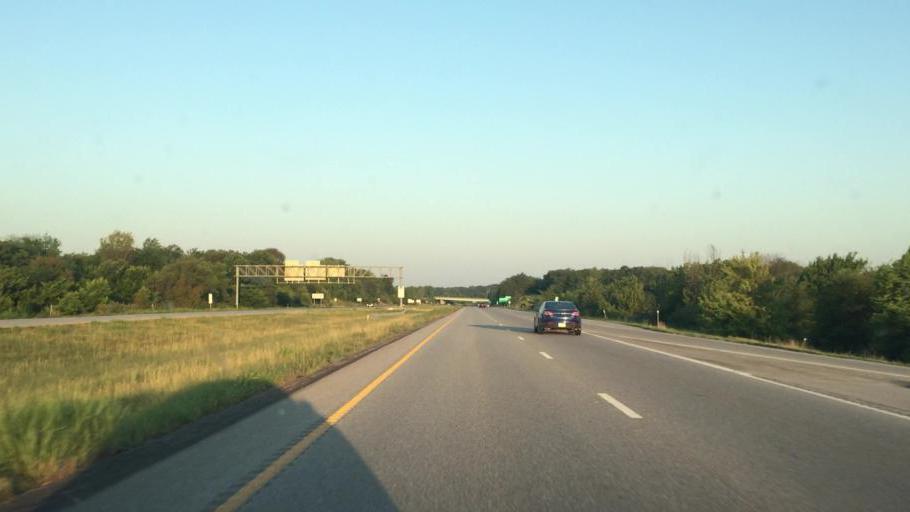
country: US
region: Missouri
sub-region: Clay County
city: Smithville
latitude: 39.3089
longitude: -94.5902
